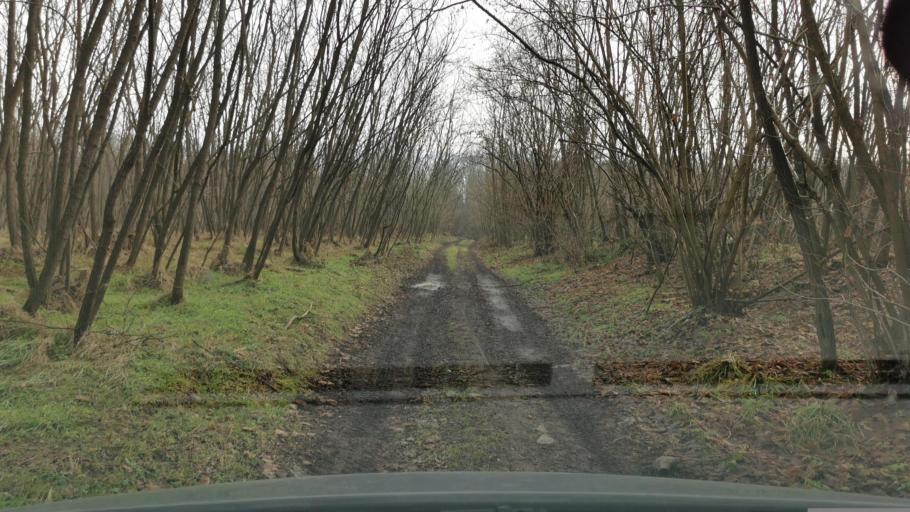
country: IT
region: Piedmont
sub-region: Provincia di Torino
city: Bosconero
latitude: 45.2562
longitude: 7.7874
